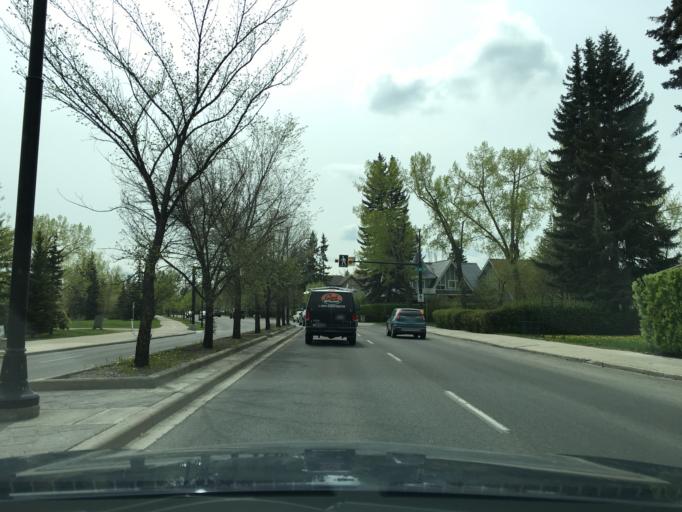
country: CA
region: Alberta
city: Calgary
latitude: 51.0255
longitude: -114.0788
